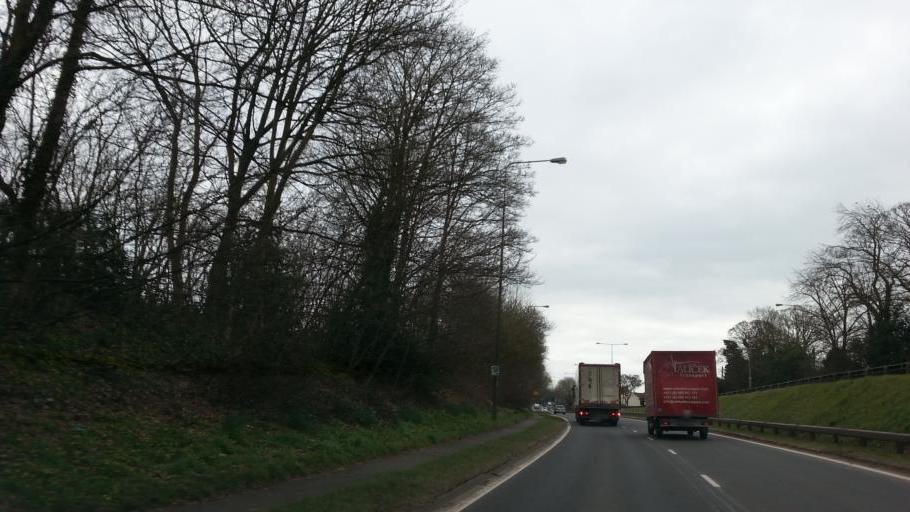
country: GB
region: England
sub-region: Staffordshire
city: Stone
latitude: 52.9014
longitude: -2.1575
